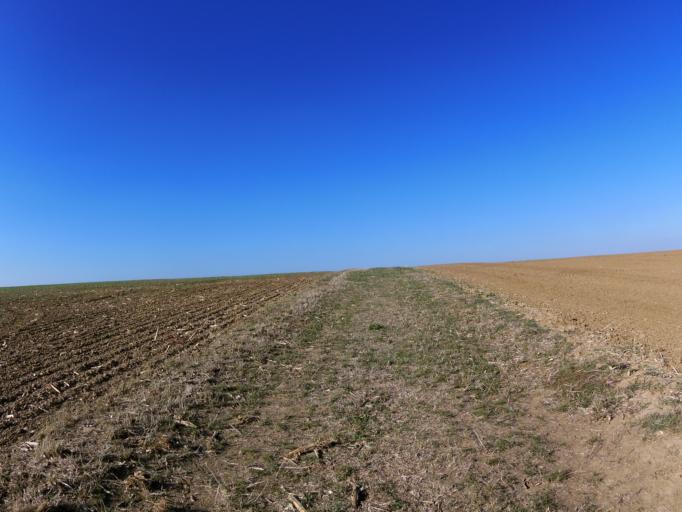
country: DE
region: Bavaria
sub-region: Regierungsbezirk Unterfranken
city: Eibelstadt
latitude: 49.7084
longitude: 9.9764
